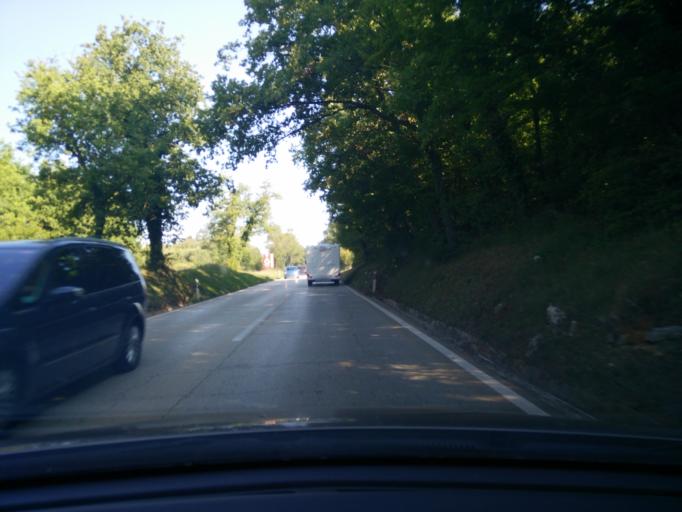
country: HR
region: Istarska
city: Novigrad
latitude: 45.2895
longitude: 13.6211
